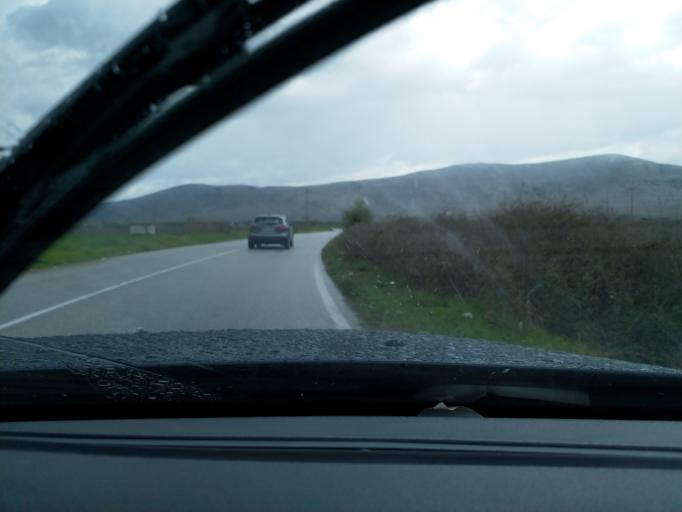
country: GR
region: Thessaly
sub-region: Trikala
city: Taxiarches
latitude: 39.5553
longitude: 21.8901
